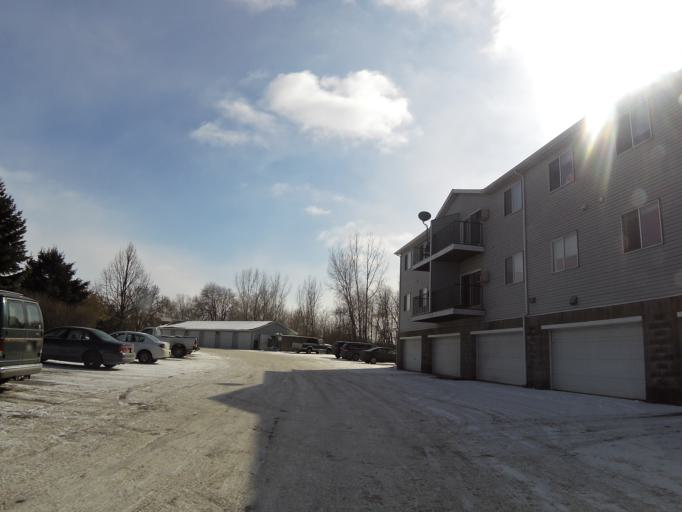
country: US
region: Minnesota
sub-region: Washington County
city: Oakdale
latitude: 44.9476
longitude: -92.9701
